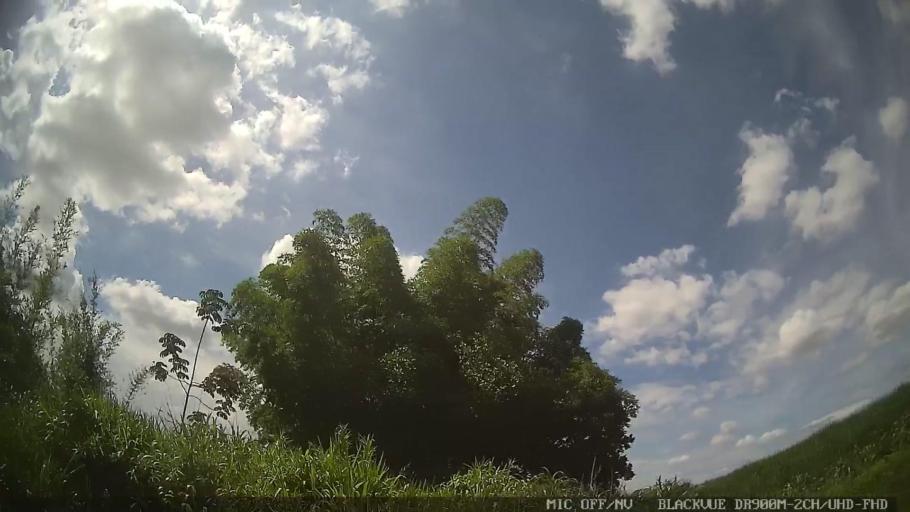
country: BR
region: Sao Paulo
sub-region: Artur Nogueira
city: Artur Nogueira
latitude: -22.5876
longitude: -47.0776
